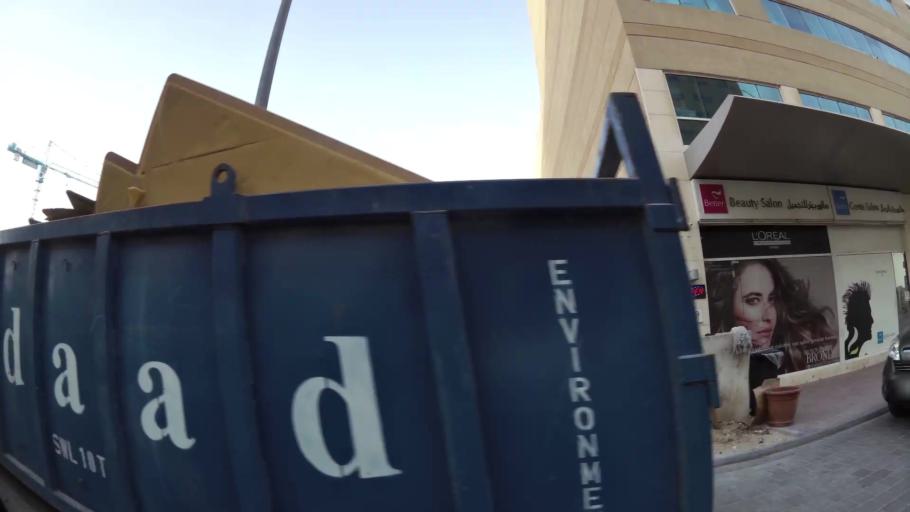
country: AE
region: Dubai
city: Dubai
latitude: 25.0666
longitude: 55.2104
